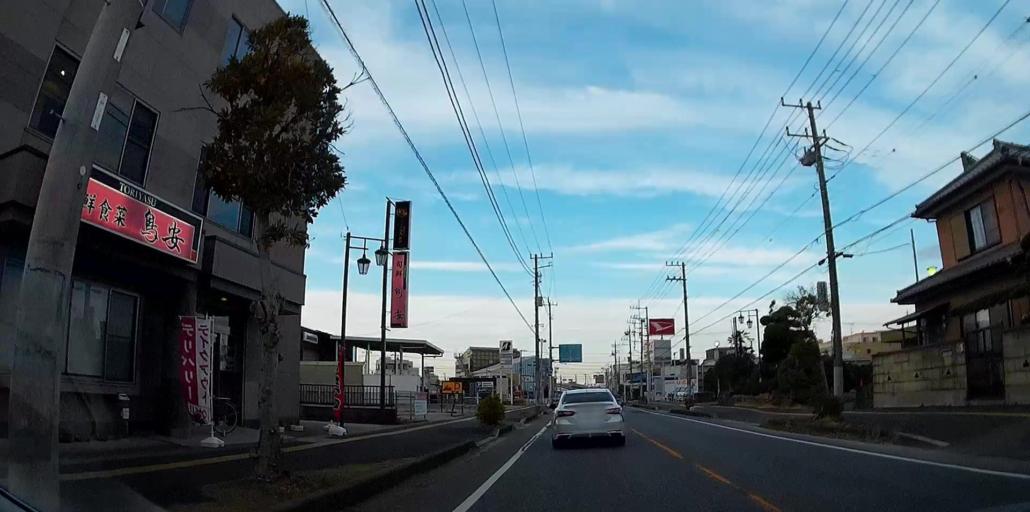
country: JP
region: Chiba
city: Ichihara
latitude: 35.4771
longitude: 140.0447
